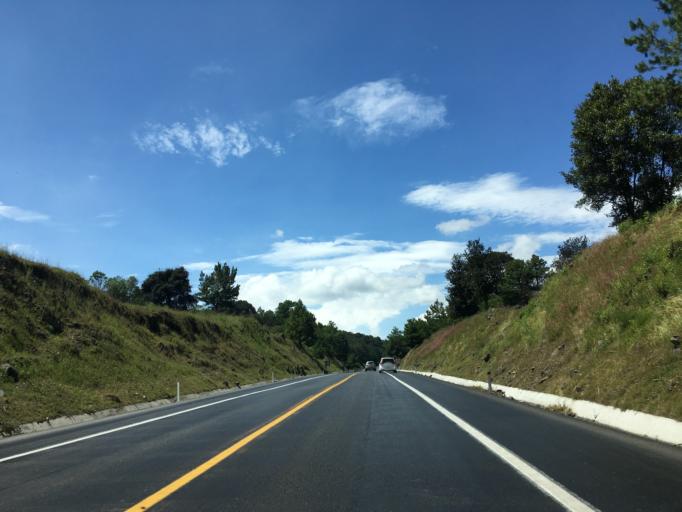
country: MX
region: Michoacan
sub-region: Patzcuaro
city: Santa Maria Huiramangaro (San Juan Tumbio)
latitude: 19.4905
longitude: -101.7104
